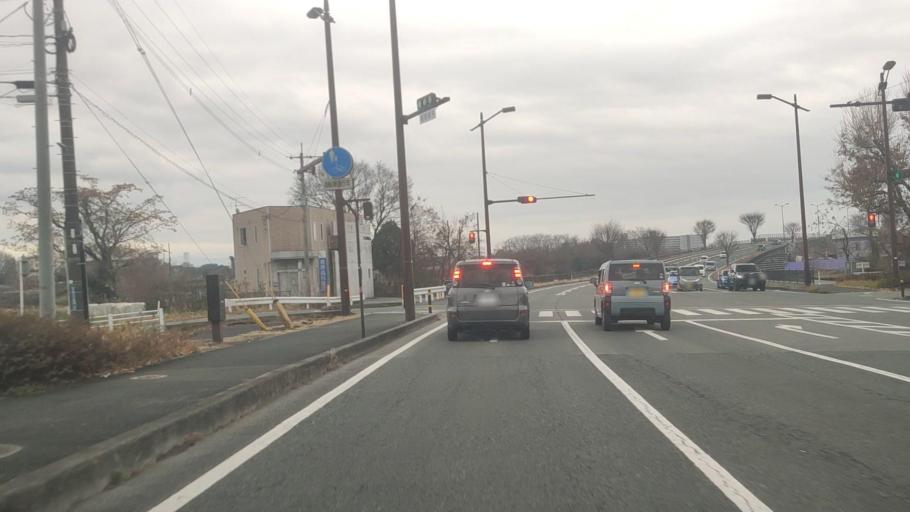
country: JP
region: Kumamoto
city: Ozu
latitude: 32.8217
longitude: 130.7911
